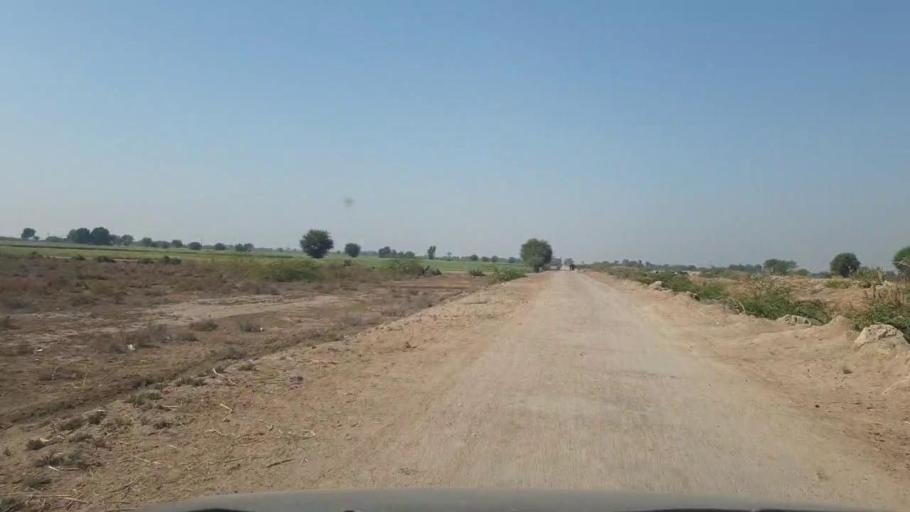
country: PK
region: Sindh
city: Digri
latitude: 25.2746
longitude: 69.2216
